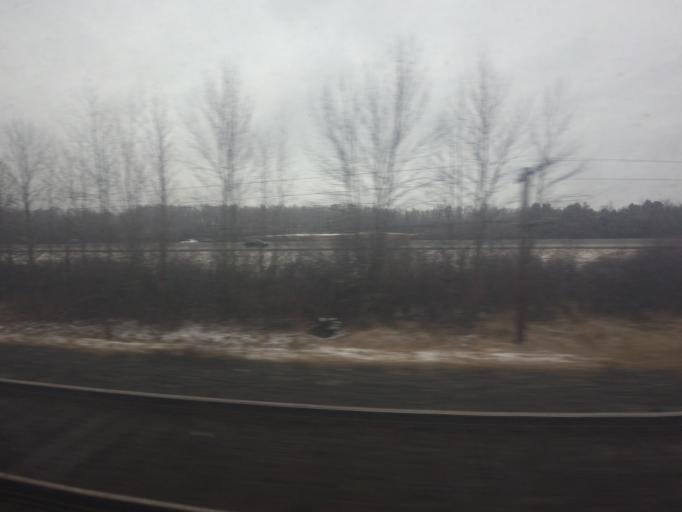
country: CA
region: Ontario
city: Kingston
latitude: 44.3111
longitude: -76.3937
